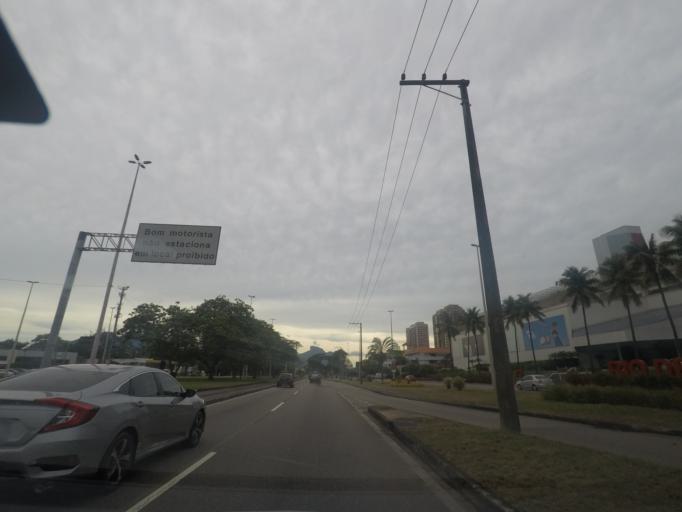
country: BR
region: Rio de Janeiro
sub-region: Nilopolis
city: Nilopolis
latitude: -23.0006
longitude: -43.3866
